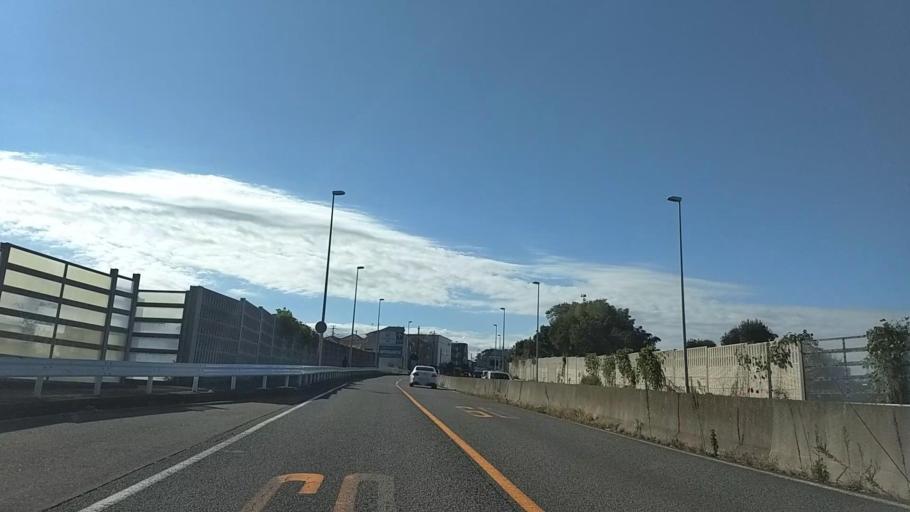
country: JP
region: Kanagawa
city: Fujisawa
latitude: 35.4098
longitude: 139.5308
